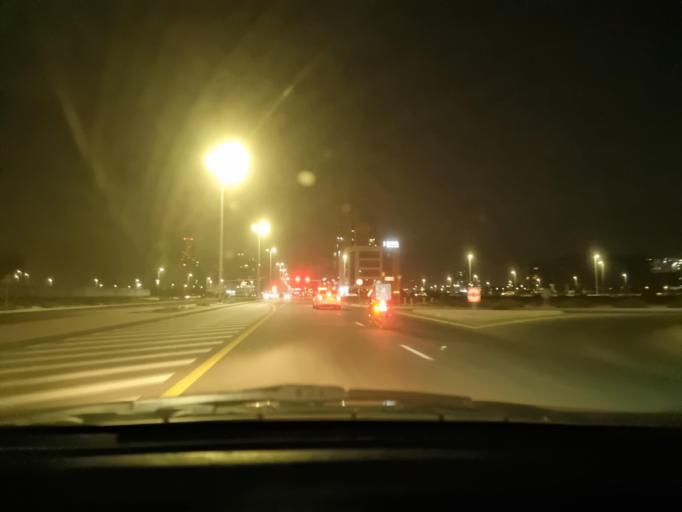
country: AE
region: Dubai
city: Dubai
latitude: 25.0929
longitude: 55.3219
